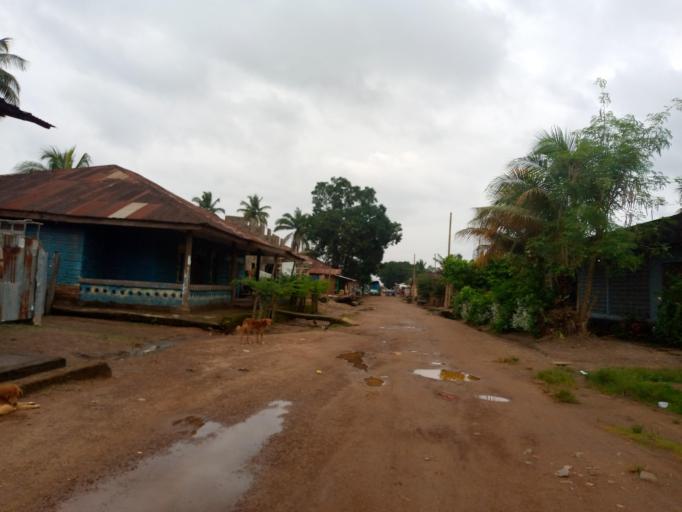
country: SL
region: Eastern Province
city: Kenema
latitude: 7.8858
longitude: -11.1860
